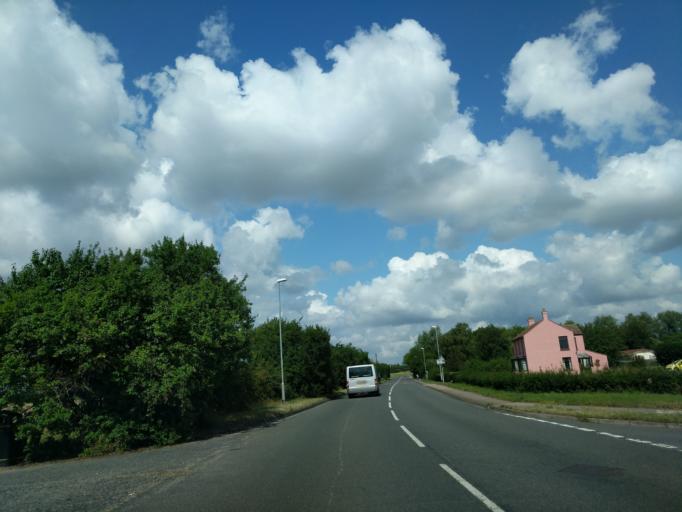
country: GB
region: England
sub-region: Cambridgeshire
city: Soham
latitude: 52.3137
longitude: 0.3747
